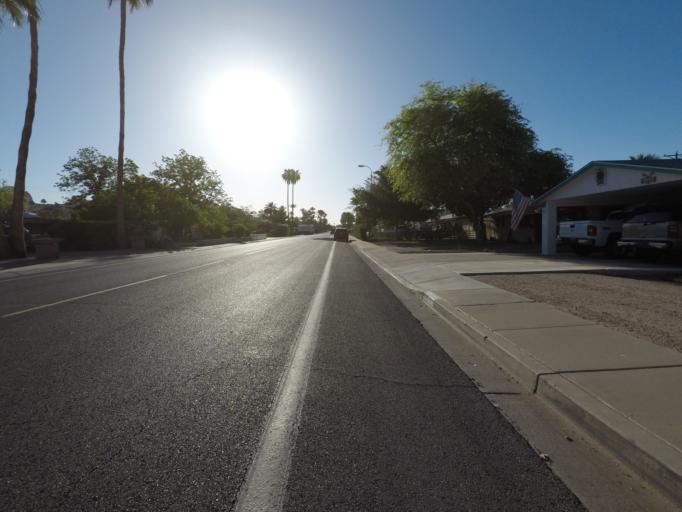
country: US
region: Arizona
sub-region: Maricopa County
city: Paradise Valley
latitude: 33.5024
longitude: -111.9925
